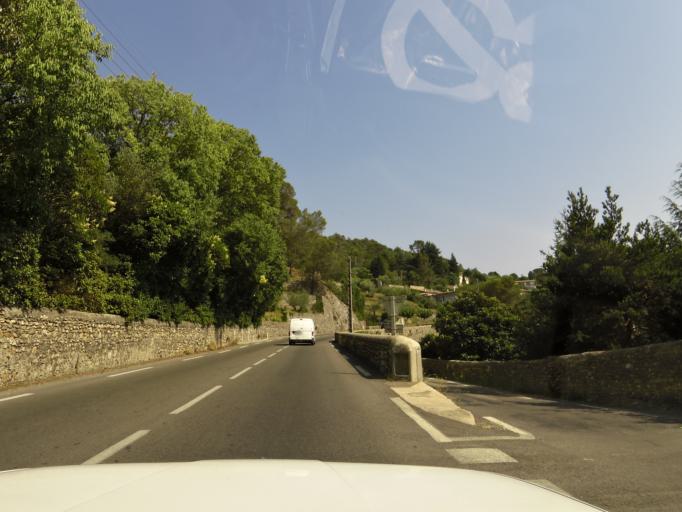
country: FR
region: Languedoc-Roussillon
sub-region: Departement du Gard
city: Anduze
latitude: 44.0548
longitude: 3.9908
